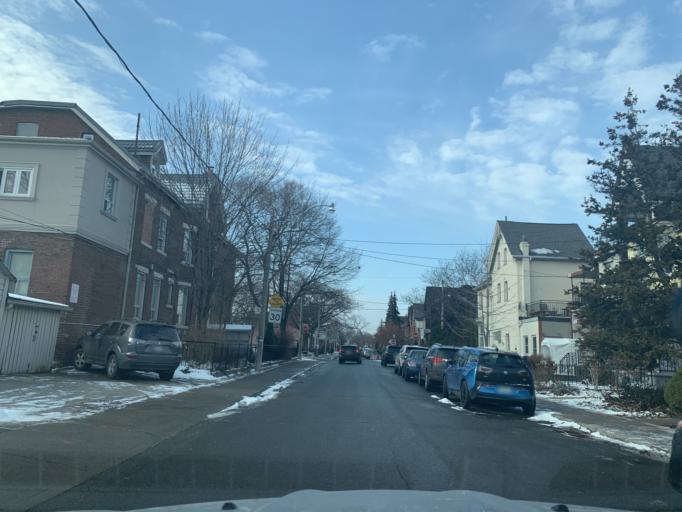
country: CA
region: Ontario
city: Toronto
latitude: 43.6607
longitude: -79.4047
